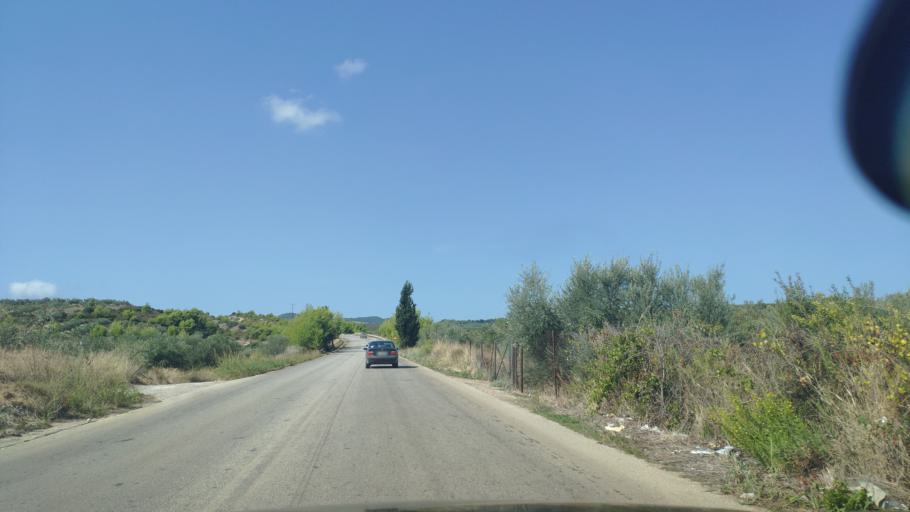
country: GR
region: Peloponnese
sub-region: Nomos Korinthias
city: Moulki
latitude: 37.9899
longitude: 22.6943
